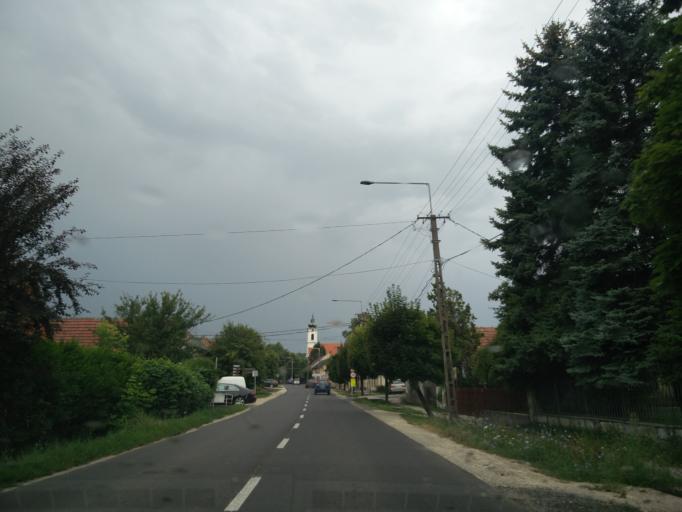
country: HU
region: Fejer
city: Etyek
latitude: 47.4469
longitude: 18.7545
